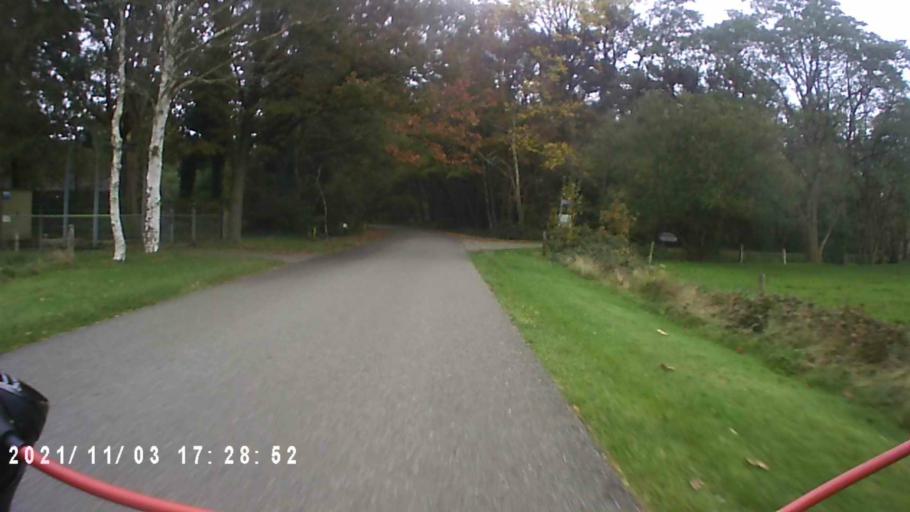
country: NL
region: Friesland
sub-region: Gemeente Weststellingwerf
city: Noordwolde
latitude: 52.8868
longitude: 6.2494
